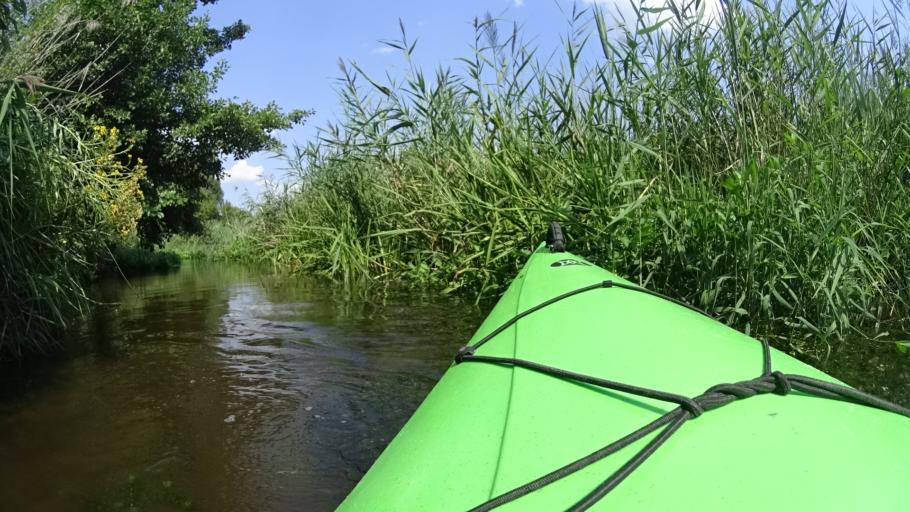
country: PL
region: Masovian Voivodeship
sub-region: Powiat bialobrzeski
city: Wysmierzyce
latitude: 51.6534
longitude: 20.8224
